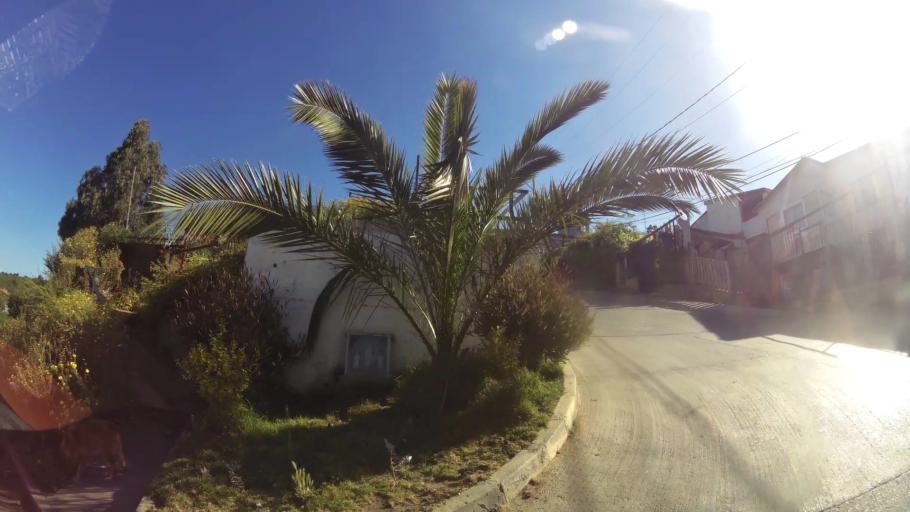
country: CL
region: Valparaiso
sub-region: Provincia de Valparaiso
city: Valparaiso
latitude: -33.0620
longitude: -71.6227
